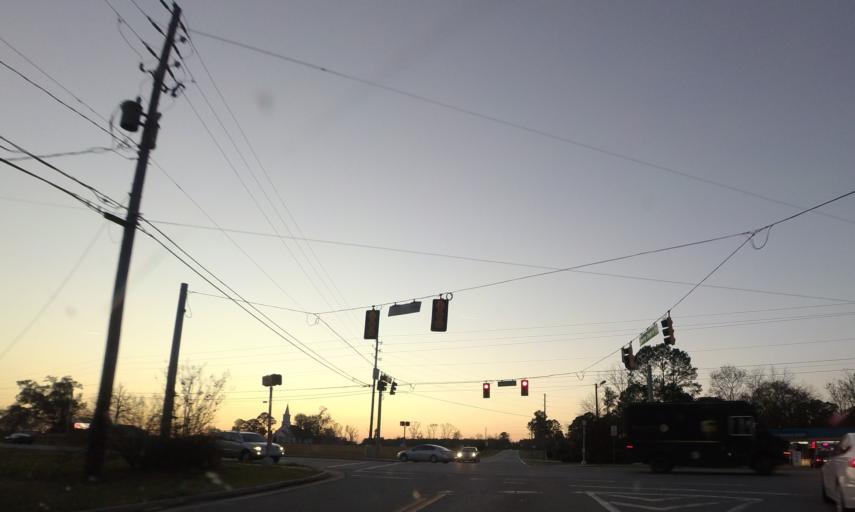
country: US
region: Georgia
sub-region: Houston County
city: Centerville
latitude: 32.7249
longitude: -83.6844
